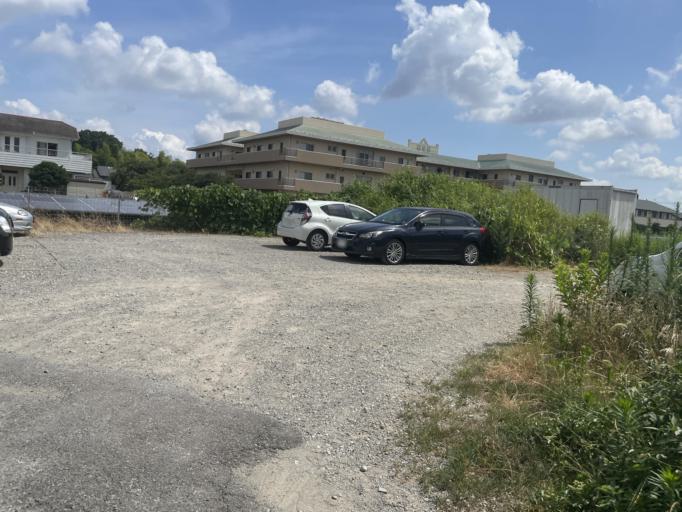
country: JP
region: Chiba
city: Kashiwa
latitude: 35.8017
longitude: 139.9654
